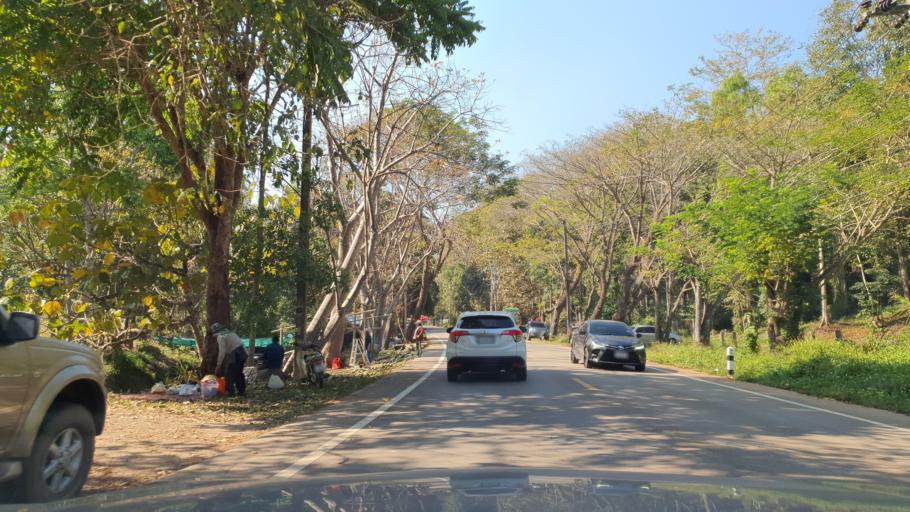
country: TH
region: Chiang Rai
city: Mae Lao
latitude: 19.8653
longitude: 99.6509
